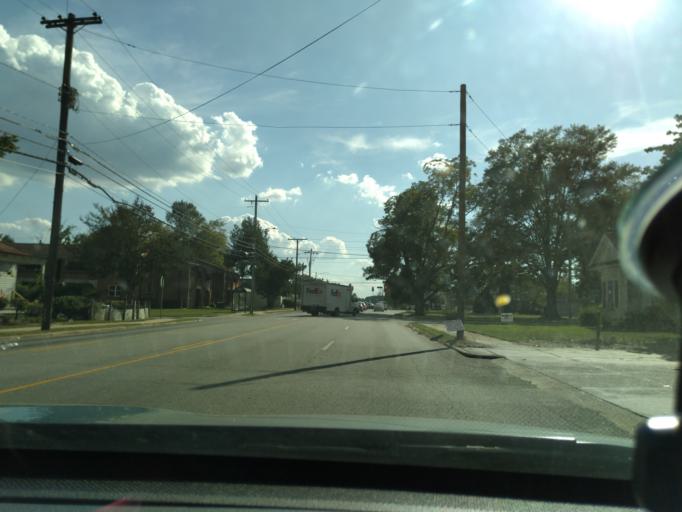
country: US
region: North Carolina
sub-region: Nash County
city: Rocky Mount
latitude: 35.9296
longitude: -77.8148
